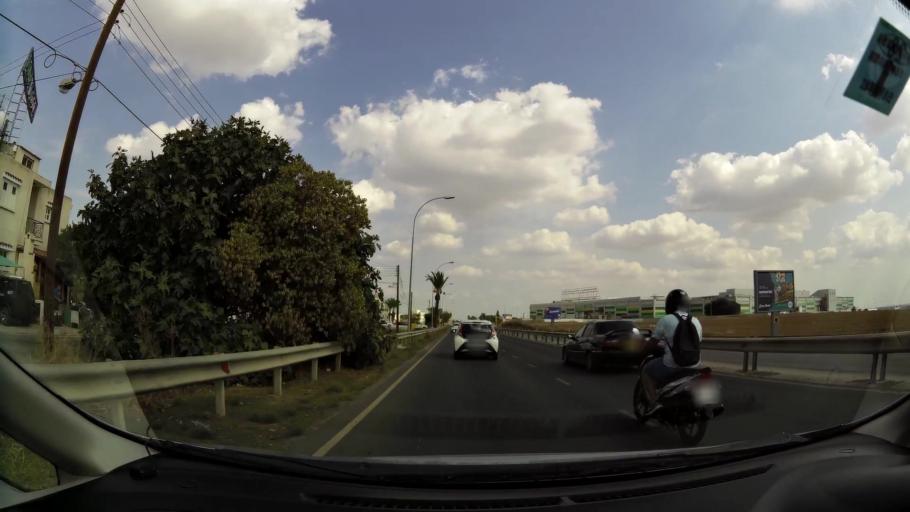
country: CY
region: Lefkosia
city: Nicosia
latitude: 35.1253
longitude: 33.3509
